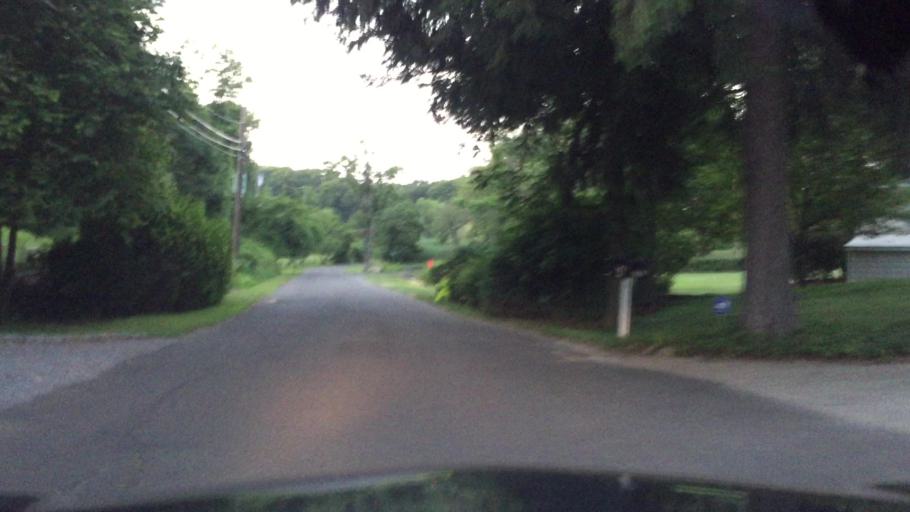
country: US
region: Connecticut
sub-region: Fairfield County
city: Darien
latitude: 41.0707
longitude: -73.4263
